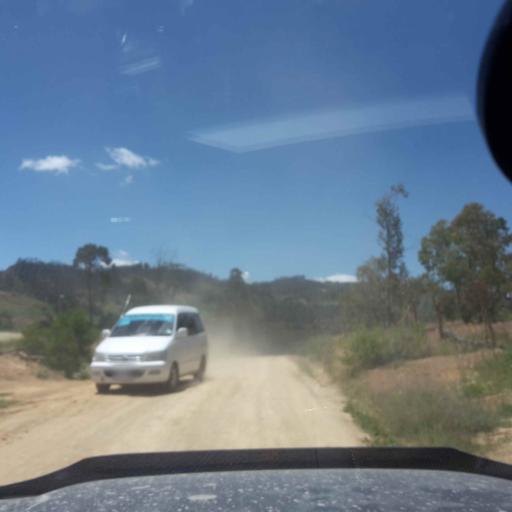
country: BO
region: Cochabamba
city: Totora
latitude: -17.7631
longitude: -65.2332
